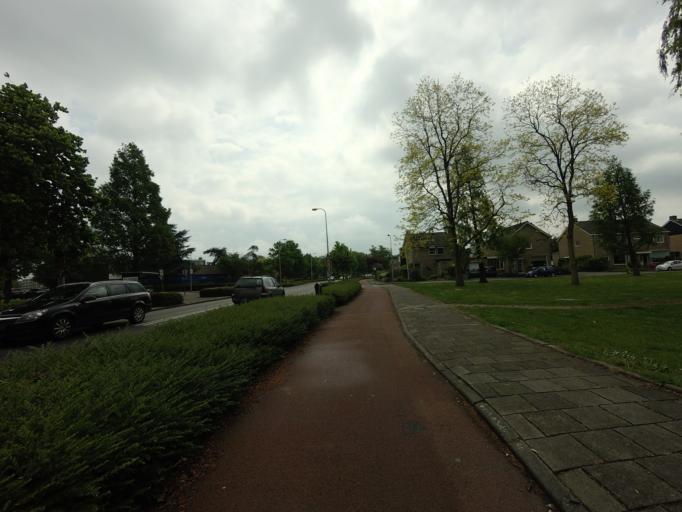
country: NL
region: South Holland
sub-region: Gemeente Ridderkerk
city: Ridderkerk
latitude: 51.8706
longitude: 4.5910
